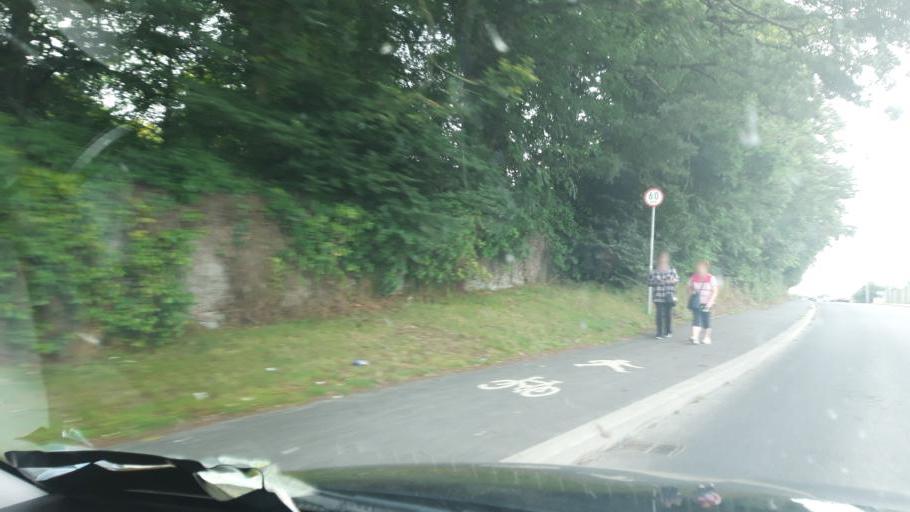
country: IE
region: Leinster
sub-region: Kilkenny
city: Kilkenny
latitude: 52.6377
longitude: -7.2707
